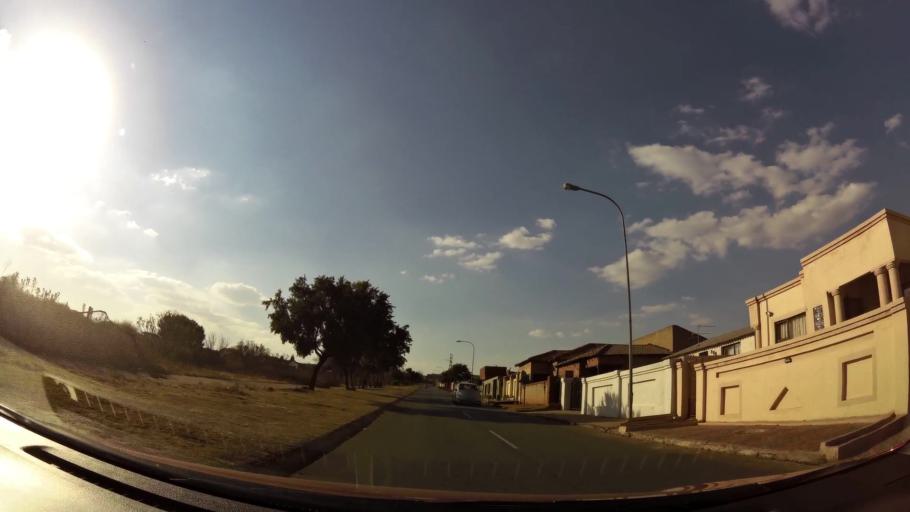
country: ZA
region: Gauteng
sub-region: City of Johannesburg Metropolitan Municipality
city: Roodepoort
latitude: -26.2056
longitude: 27.8783
